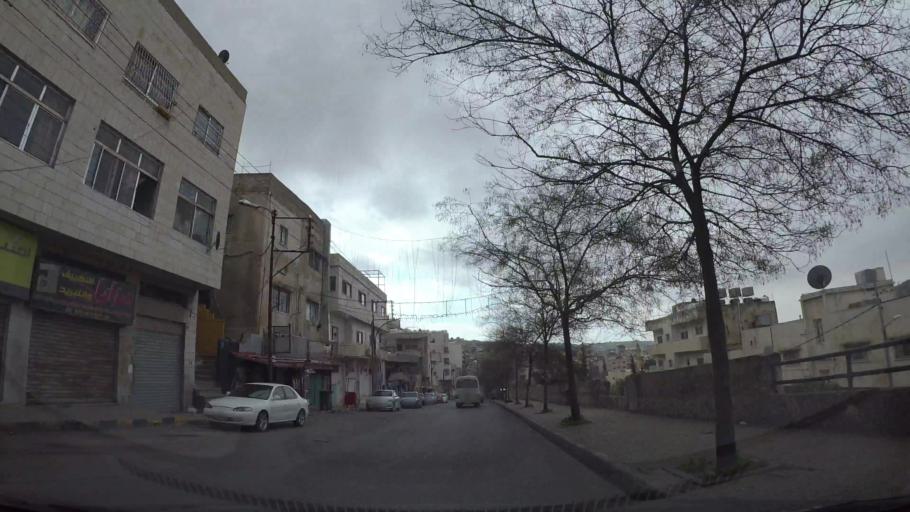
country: JO
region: Amman
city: Wadi as Sir
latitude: 31.9512
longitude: 35.8193
